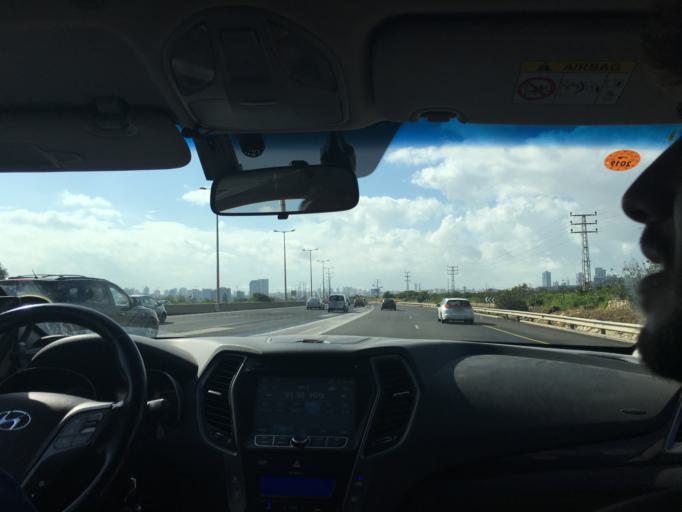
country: IL
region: Tel Aviv
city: Ramat HaSharon
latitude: 32.1216
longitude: 34.8531
